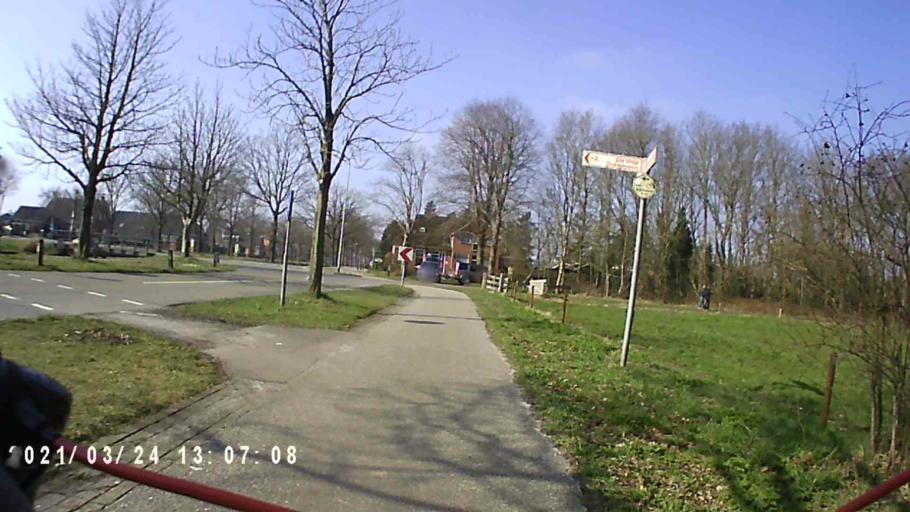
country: NL
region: Groningen
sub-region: Gemeente Leek
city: Leek
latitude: 53.1297
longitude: 6.3042
